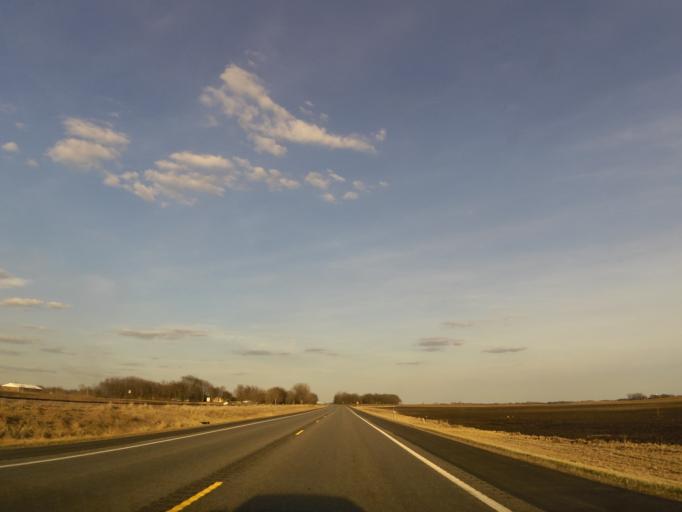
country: US
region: Minnesota
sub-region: McLeod County
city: Glencoe
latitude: 44.7393
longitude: -94.2693
